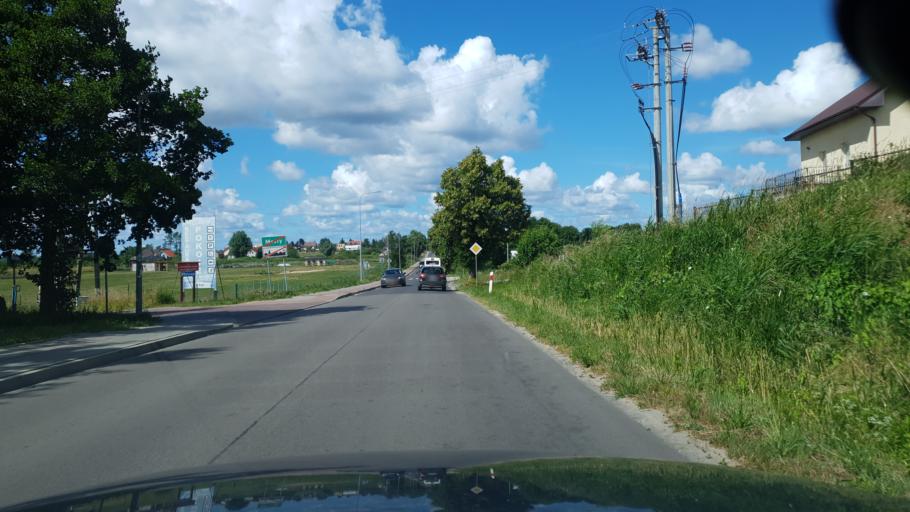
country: PL
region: Pomeranian Voivodeship
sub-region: Powiat pucki
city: Mosty
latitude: 54.6219
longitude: 18.4964
